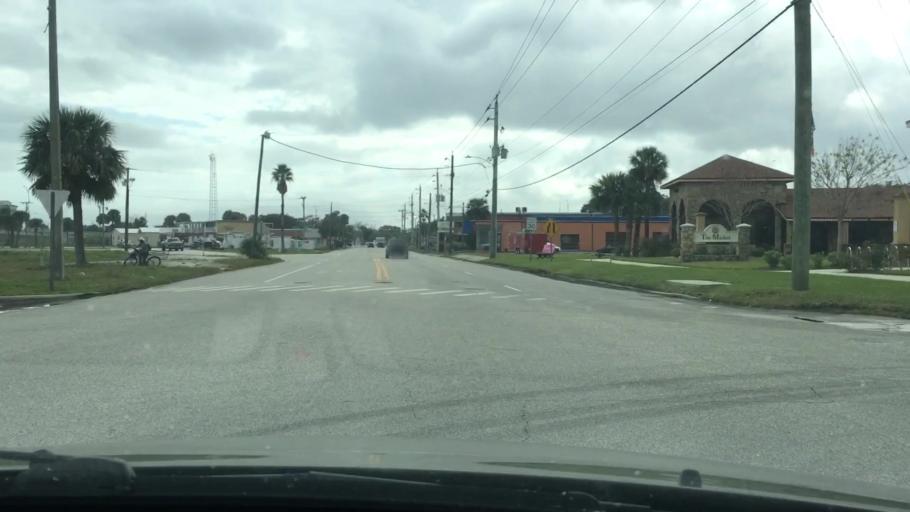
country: US
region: Florida
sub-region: Volusia County
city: Holly Hill
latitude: 29.2308
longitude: -81.0286
